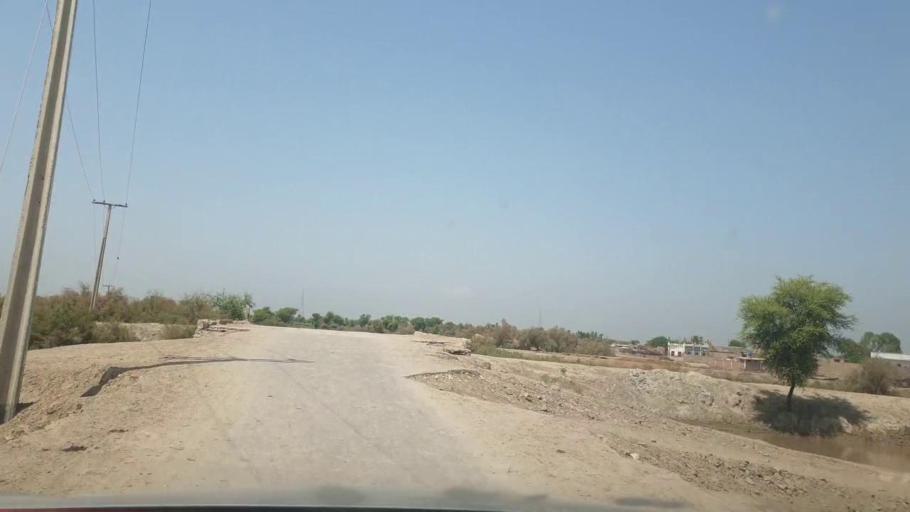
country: PK
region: Sindh
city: Warah
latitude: 27.4828
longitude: 67.7532
